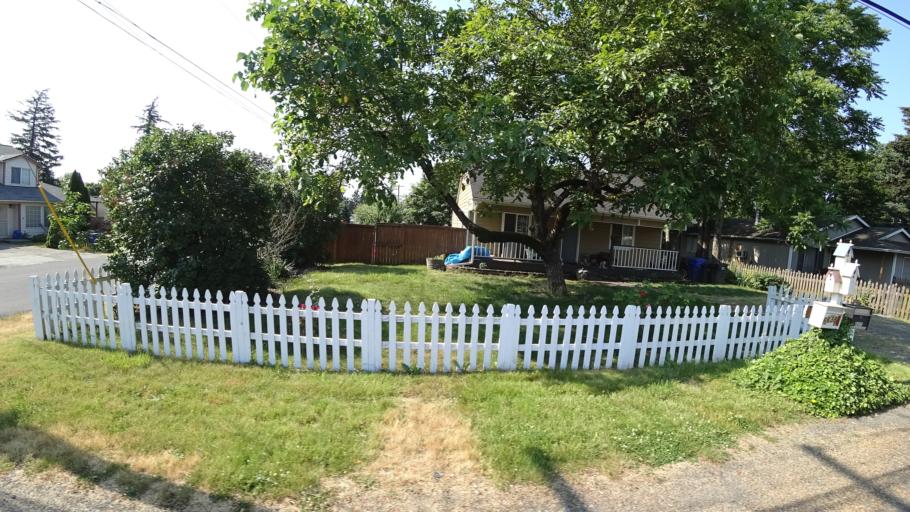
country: US
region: Oregon
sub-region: Multnomah County
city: Lents
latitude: 45.4614
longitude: -122.5948
